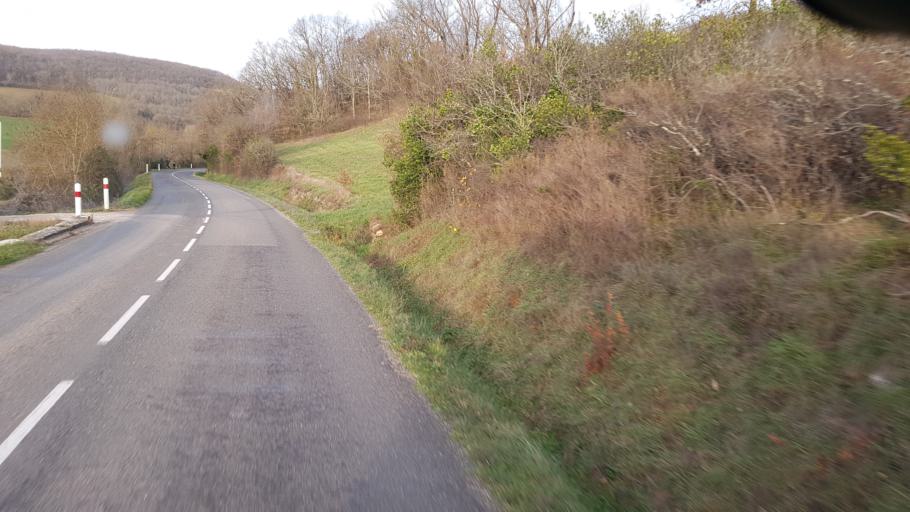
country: FR
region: Midi-Pyrenees
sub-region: Departement du Tarn-et-Garonne
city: Monclar-de-Quercy
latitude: 43.9832
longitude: 1.7159
